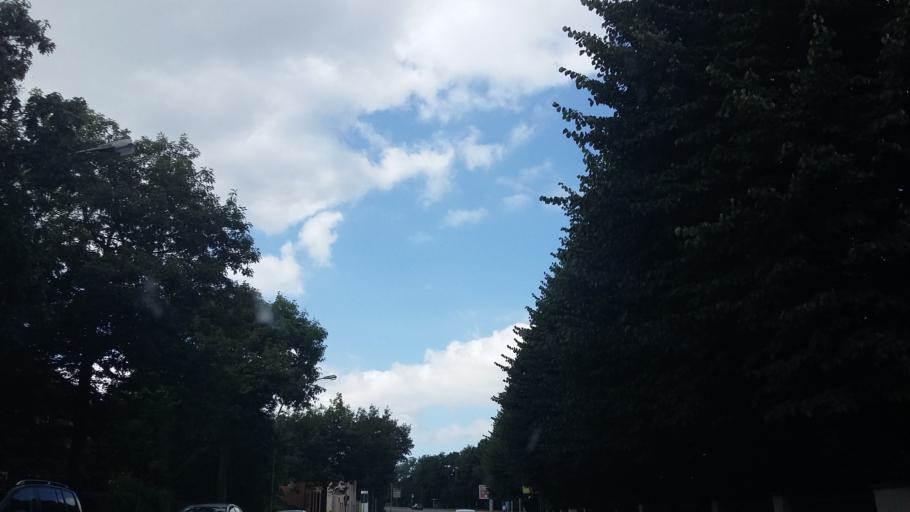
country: DE
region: Bremen
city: Bremerhaven
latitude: 53.5174
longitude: 8.5918
